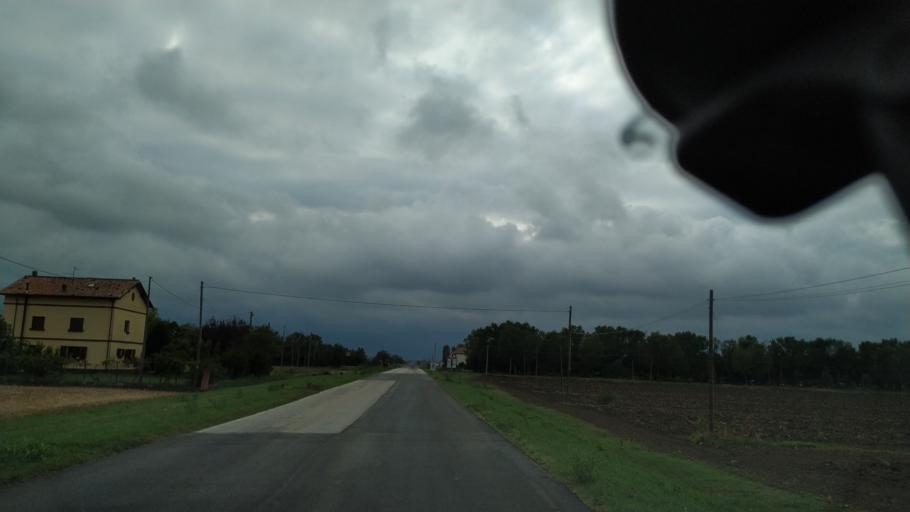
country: IT
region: Emilia-Romagna
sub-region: Provincia di Bologna
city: Decima
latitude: 44.7069
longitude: 11.2065
